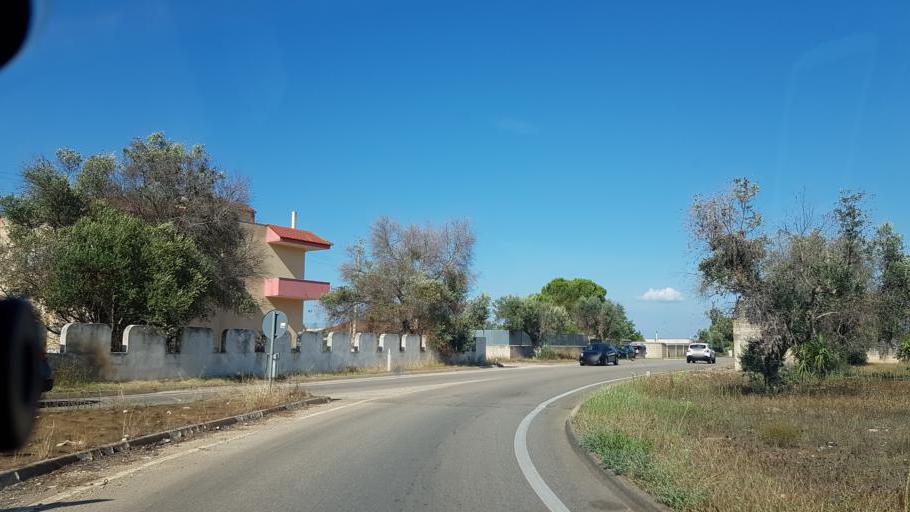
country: IT
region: Apulia
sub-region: Provincia di Lecce
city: Leverano
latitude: 40.2674
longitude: 18.0164
